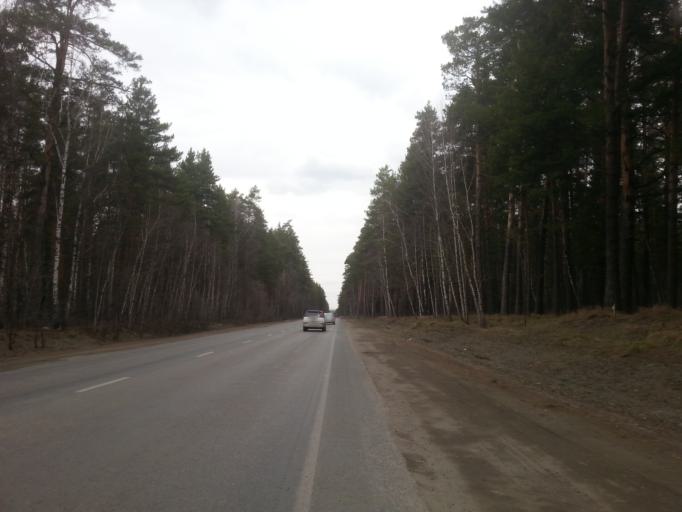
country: RU
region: Altai Krai
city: Yuzhnyy
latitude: 53.2785
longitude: 83.7185
